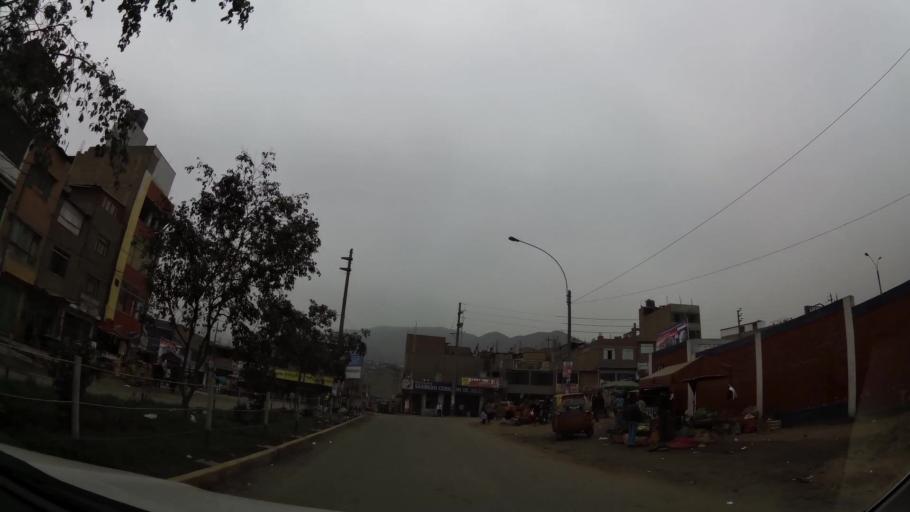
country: PE
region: Lima
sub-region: Lima
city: Urb. Santo Domingo
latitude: -11.9386
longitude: -76.9891
